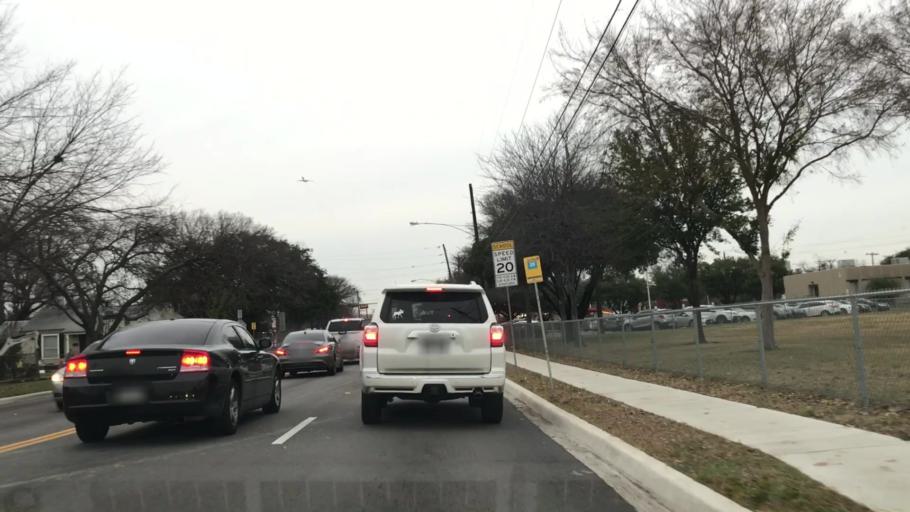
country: US
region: Texas
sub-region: Dallas County
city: Highland Park
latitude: 32.8248
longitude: -96.8300
